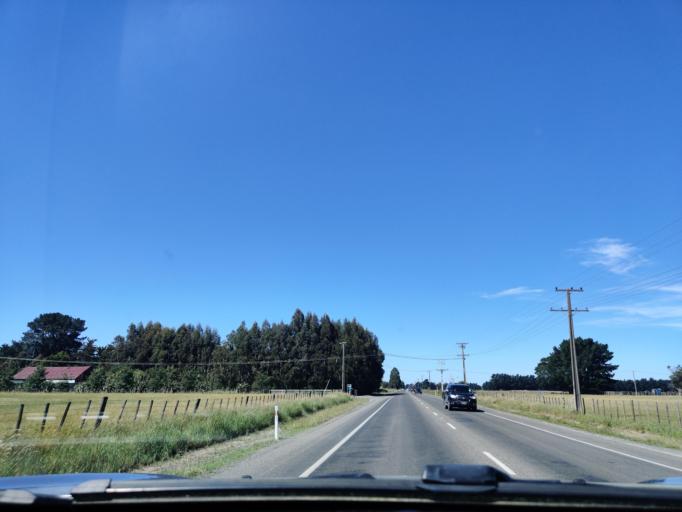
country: NZ
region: Wellington
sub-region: Masterton District
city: Masterton
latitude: -41.1016
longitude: 175.4205
